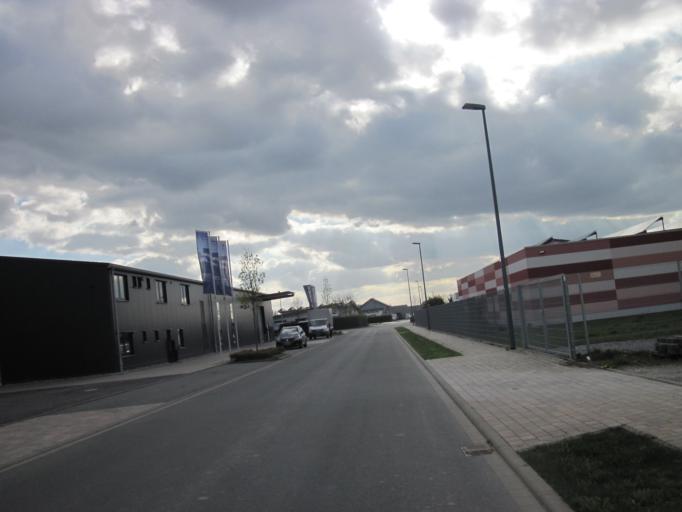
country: DE
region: North Rhine-Westphalia
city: Bad Lippspringe
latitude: 51.7691
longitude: 8.8088
